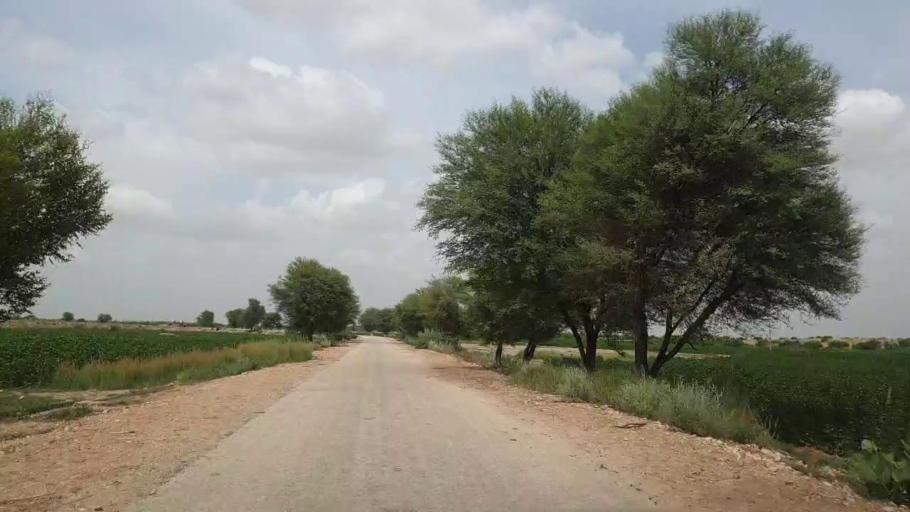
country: PK
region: Sindh
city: Kot Diji
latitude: 27.2267
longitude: 69.0879
